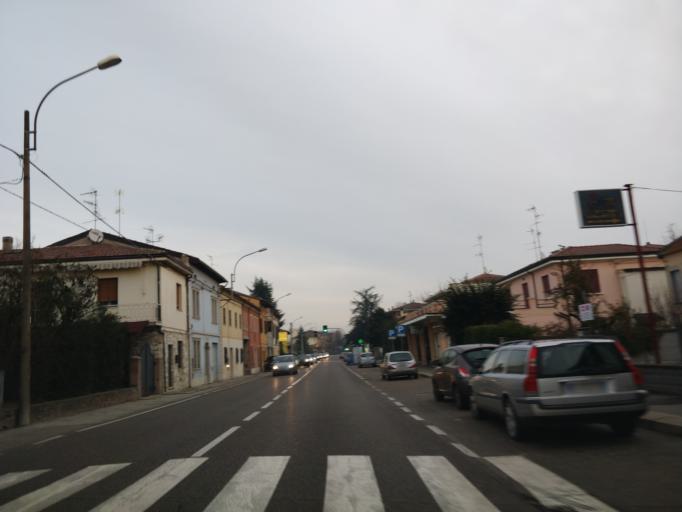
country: IT
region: Emilia-Romagna
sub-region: Provincia di Ferrara
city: Corpo Reno
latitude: 44.7580
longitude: 11.3124
